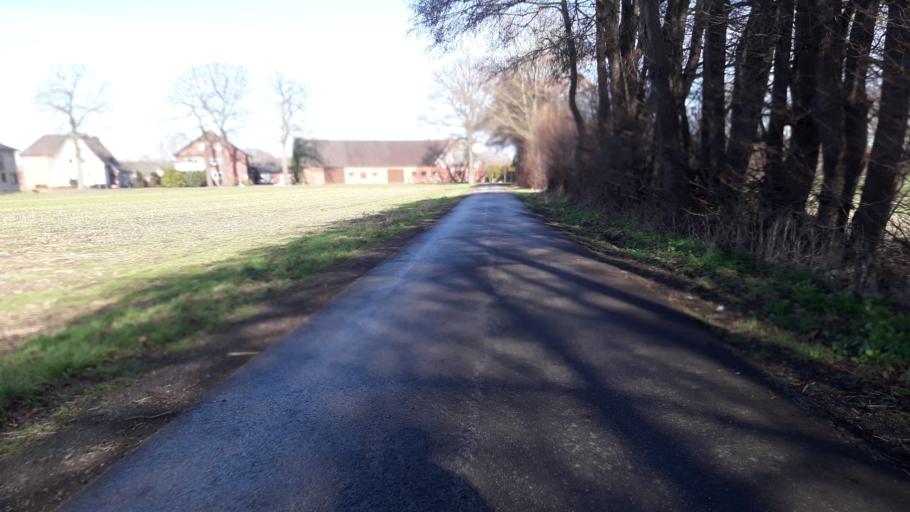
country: DE
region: North Rhine-Westphalia
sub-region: Regierungsbezirk Detmold
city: Delbruck
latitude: 51.7432
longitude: 8.5016
